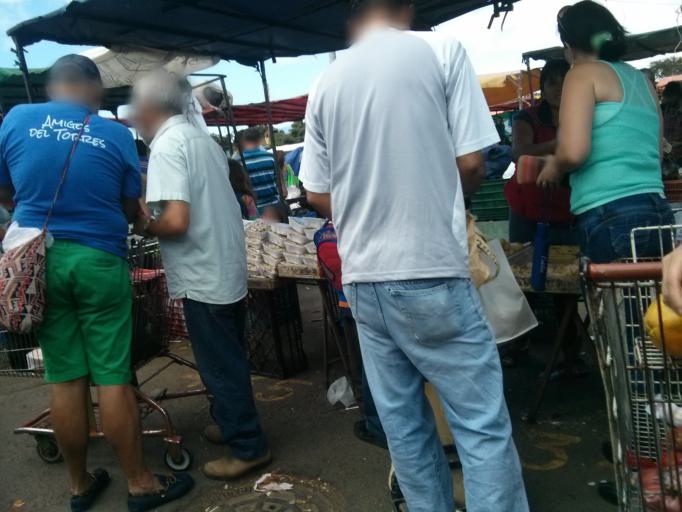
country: CR
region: San Jose
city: San Pedro
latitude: 9.9178
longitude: -84.0512
